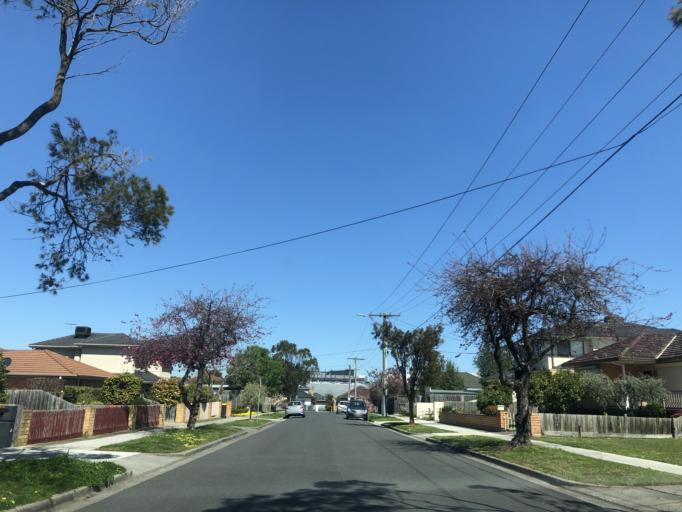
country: AU
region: Victoria
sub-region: Monash
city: Clayton
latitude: -37.9168
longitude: 145.1256
